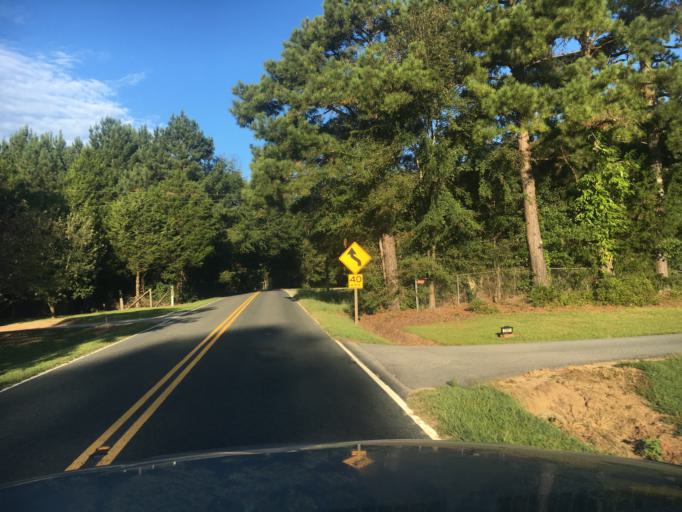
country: US
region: South Carolina
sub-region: Spartanburg County
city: Woodruff
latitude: 34.6357
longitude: -82.0014
